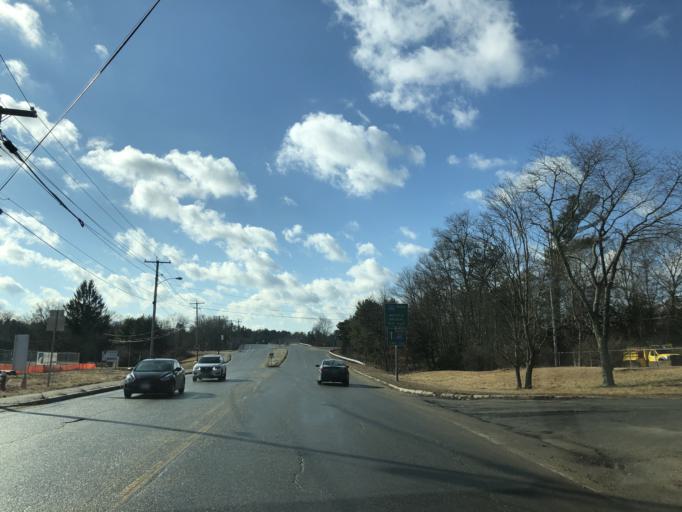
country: US
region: Massachusetts
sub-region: Bristol County
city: Norton Center
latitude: 41.9850
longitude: -71.1576
